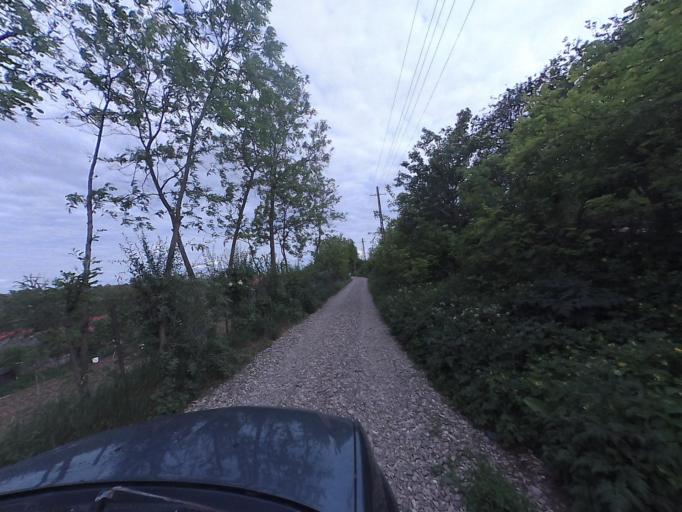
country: RO
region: Neamt
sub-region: Comuna Dulcesti
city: Dulcesti
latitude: 46.9588
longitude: 26.7866
